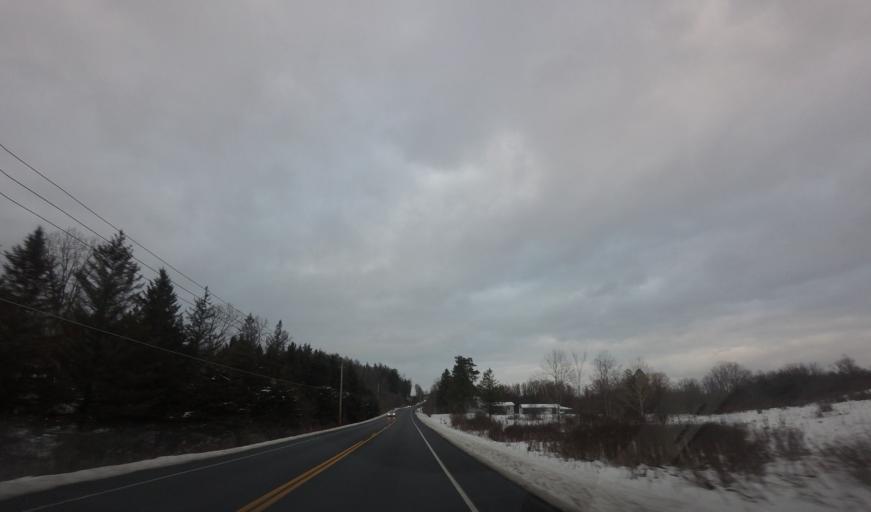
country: US
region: New York
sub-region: Tompkins County
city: Dryden
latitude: 42.5422
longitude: -76.2983
